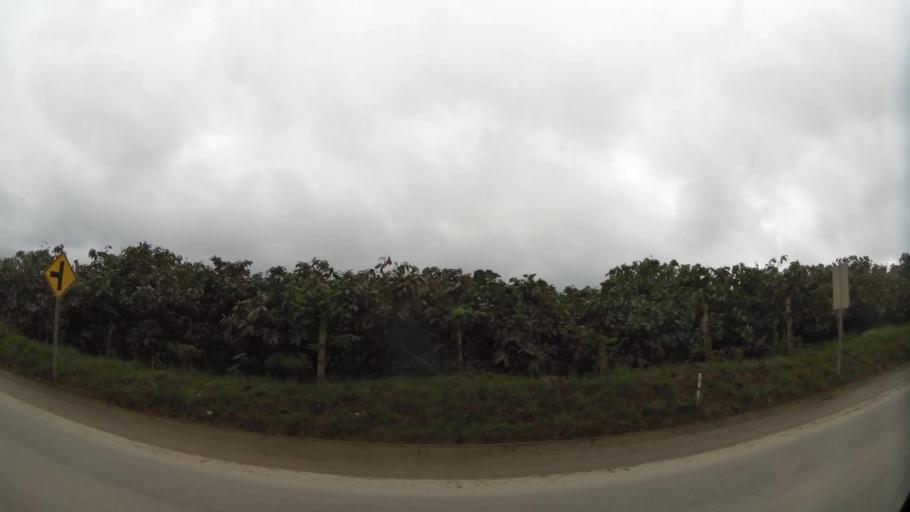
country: EC
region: El Oro
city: Pasaje
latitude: -3.3284
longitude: -79.7694
